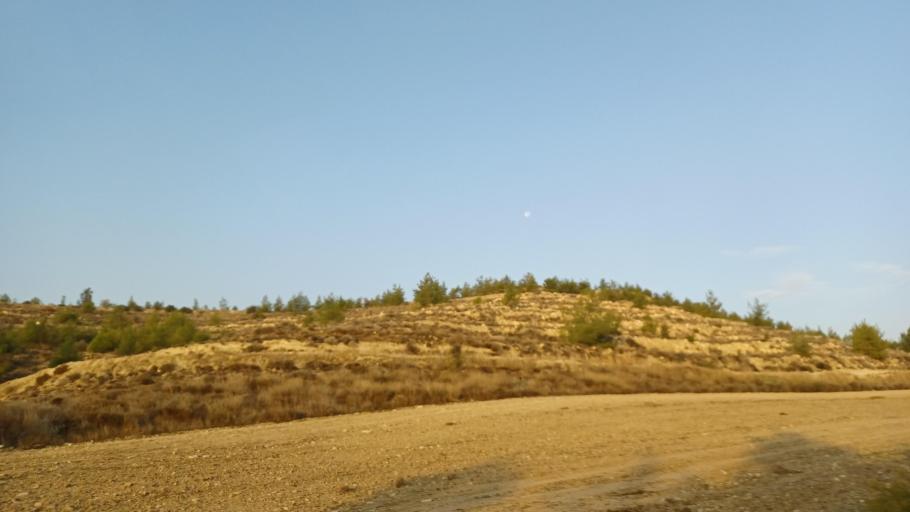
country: CY
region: Lefkosia
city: Lympia
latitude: 35.0007
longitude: 33.5247
